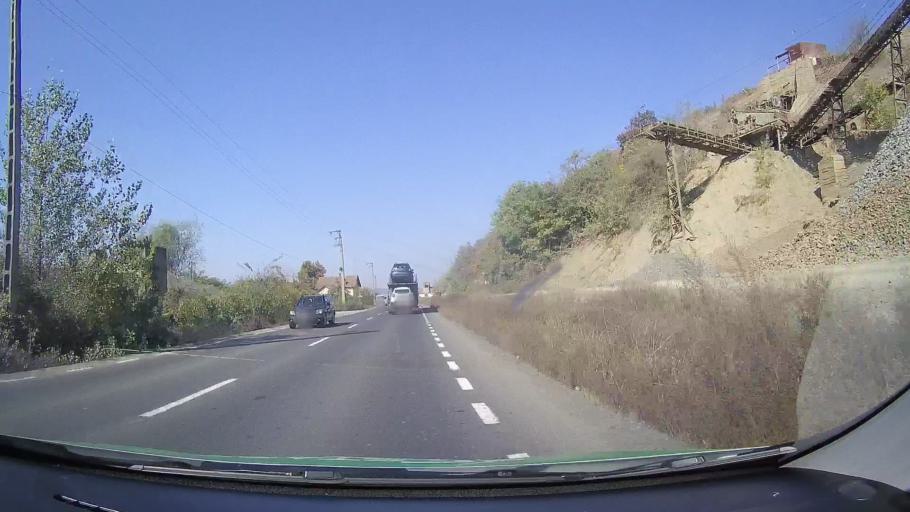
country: RO
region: Arad
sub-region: Comuna Bata
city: Bata
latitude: 46.0547
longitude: 22.0480
